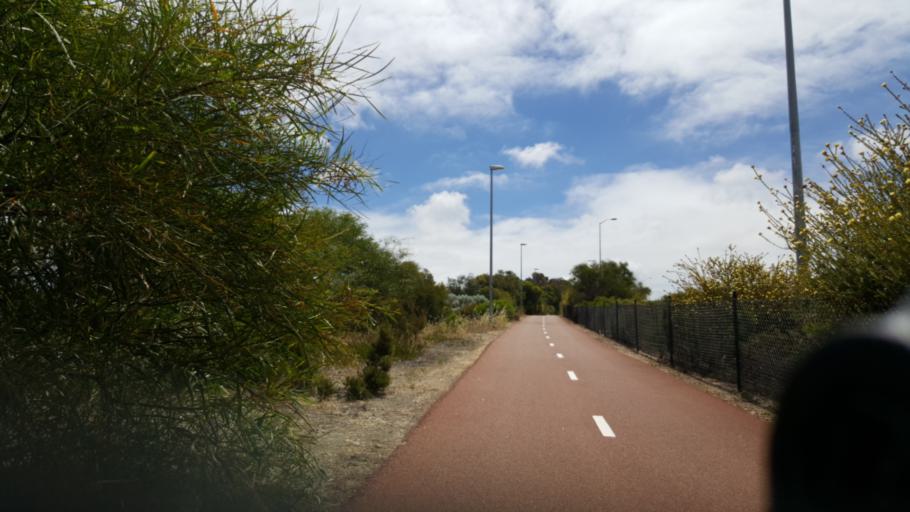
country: AU
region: Western Australia
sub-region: Stirling
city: Westminster
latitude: -31.8684
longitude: 115.8768
